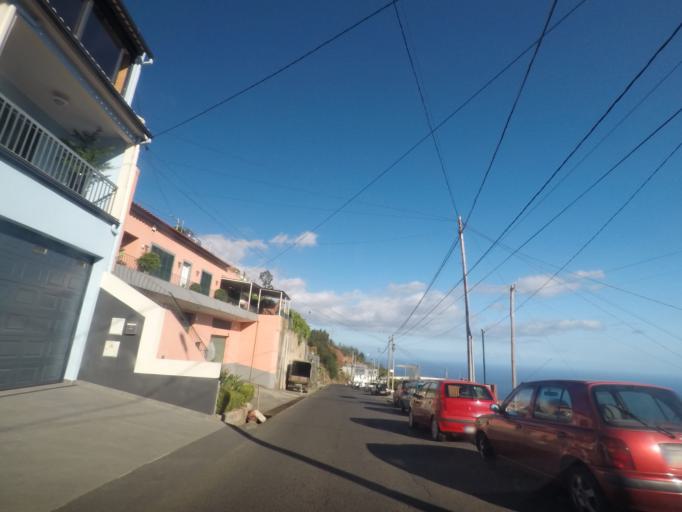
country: PT
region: Madeira
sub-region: Ribeira Brava
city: Campanario
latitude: 32.6657
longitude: -16.9976
